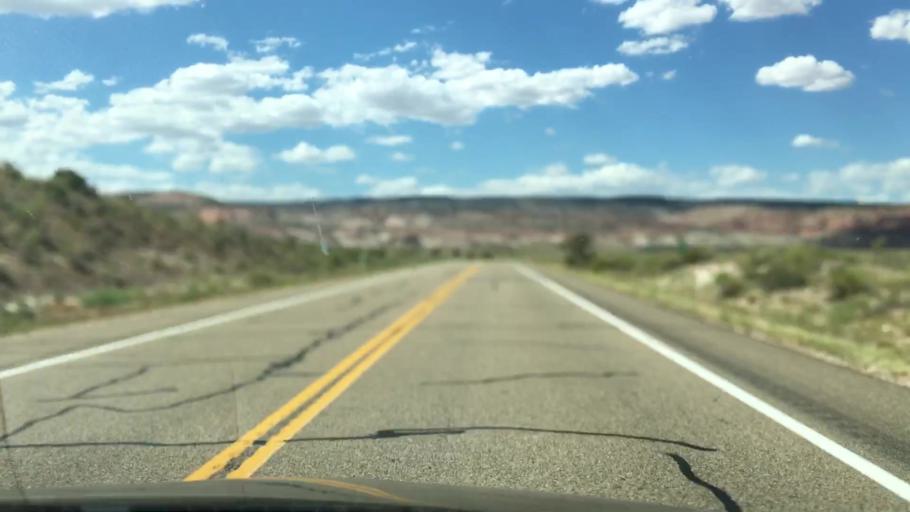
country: US
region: Arizona
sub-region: Coconino County
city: Page
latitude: 37.1097
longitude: -111.9214
